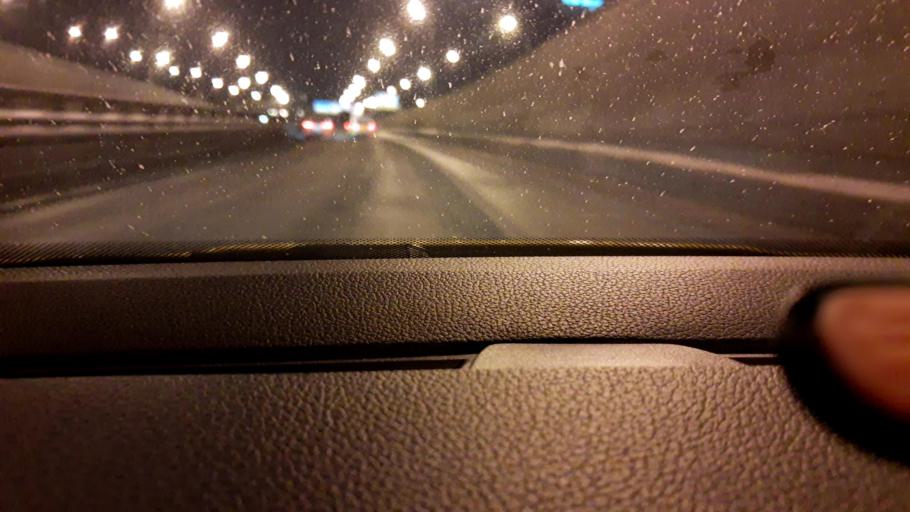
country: RU
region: Moscow
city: Rublevo
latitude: 55.7854
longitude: 37.3864
